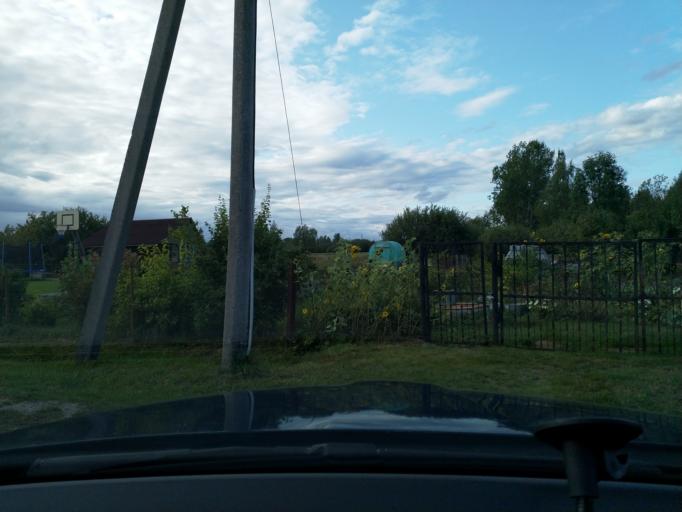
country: LV
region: Kuldigas Rajons
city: Kuldiga
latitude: 56.9534
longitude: 21.9804
